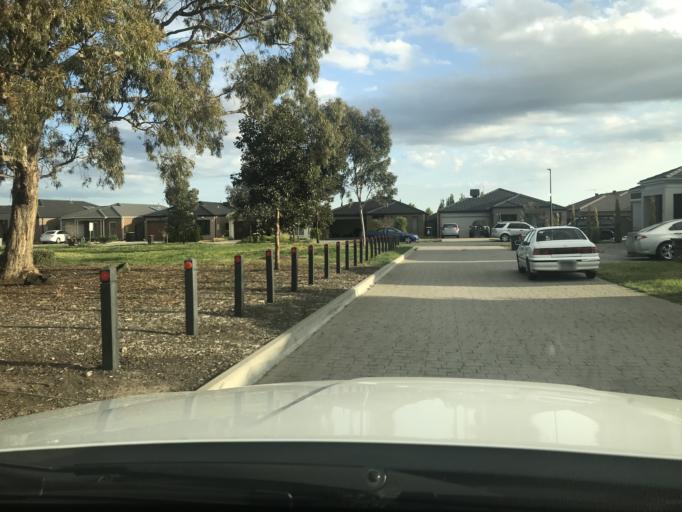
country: AU
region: Victoria
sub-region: Hume
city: Craigieburn
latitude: -37.5725
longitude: 144.9052
